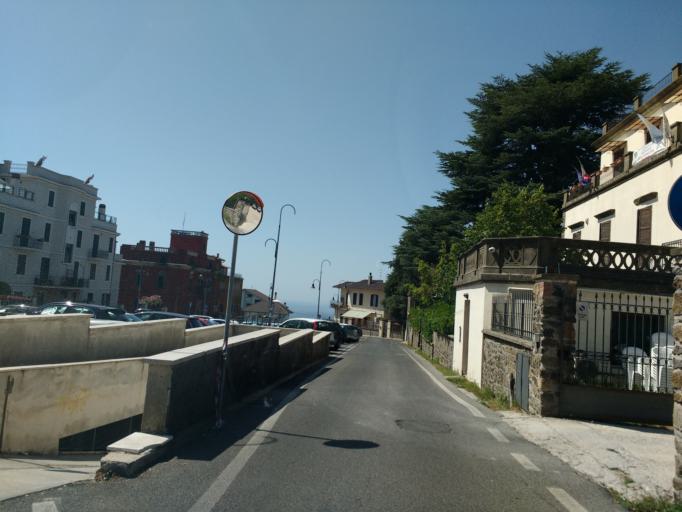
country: IT
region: Latium
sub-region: Citta metropolitana di Roma Capitale
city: Rocca di Papa
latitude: 41.7631
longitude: 12.7051
